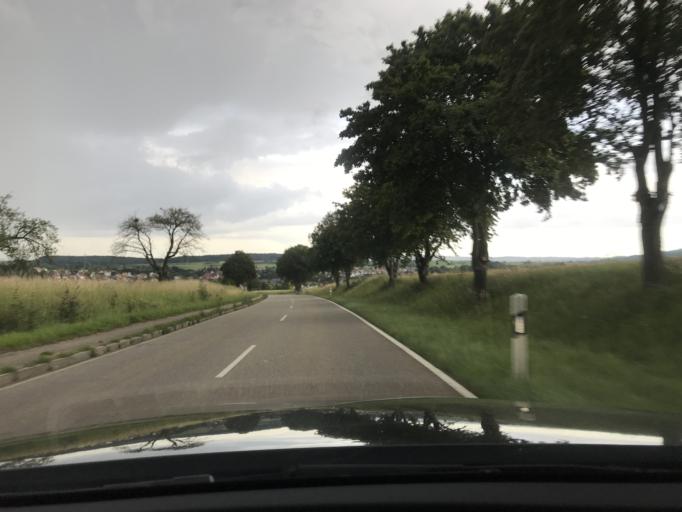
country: DE
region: Baden-Wuerttemberg
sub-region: Regierungsbezirk Stuttgart
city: Affalterbach
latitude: 48.8870
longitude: 9.3006
